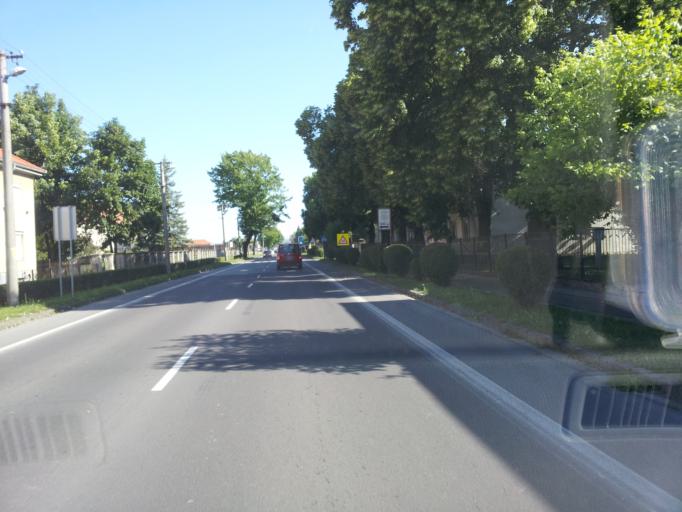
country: SK
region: Nitriansky
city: Sahy
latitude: 48.0762
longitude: 18.9465
